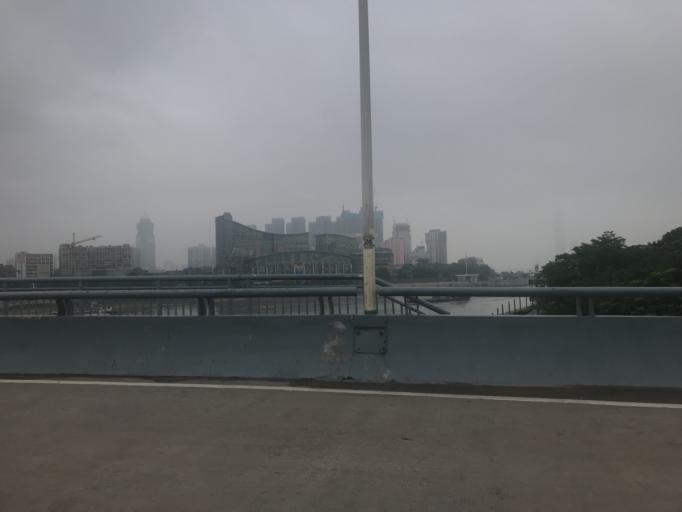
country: CN
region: Hubei
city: Wuhan
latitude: 30.5648
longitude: 114.2803
